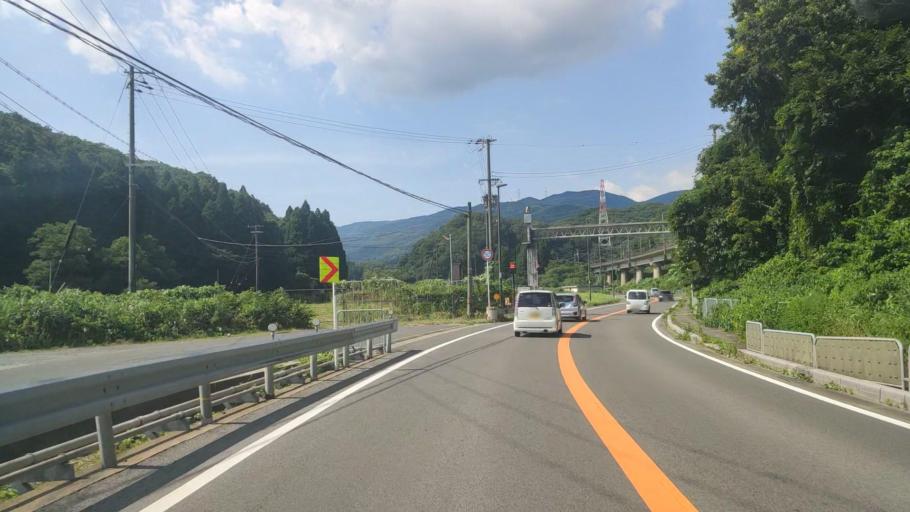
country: JP
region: Fukui
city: Tsuruga
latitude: 35.5429
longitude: 136.1494
